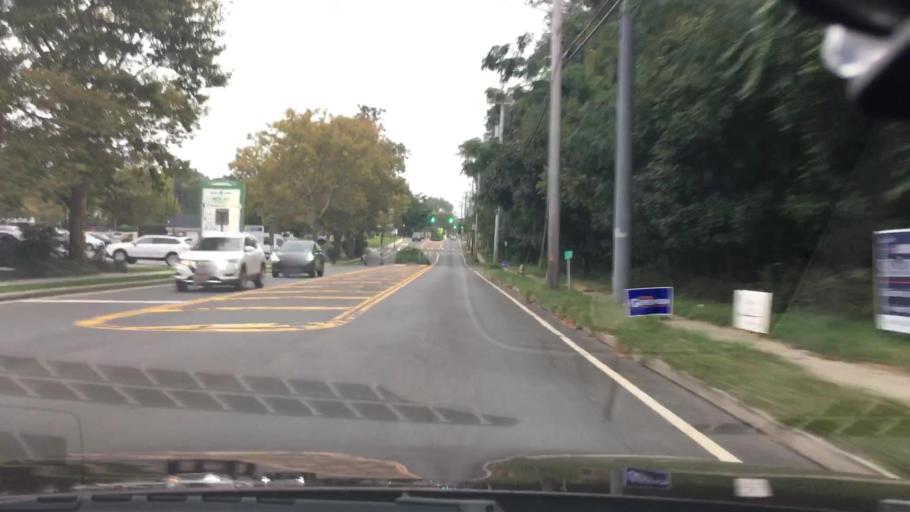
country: US
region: New York
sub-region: Suffolk County
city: East Setauket
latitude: 40.9383
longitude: -73.1099
